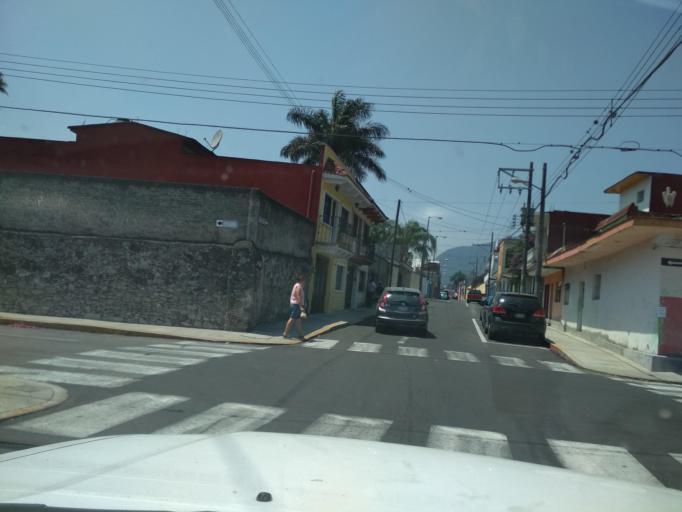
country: MX
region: Veracruz
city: Orizaba
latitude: 18.8509
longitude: -97.0881
